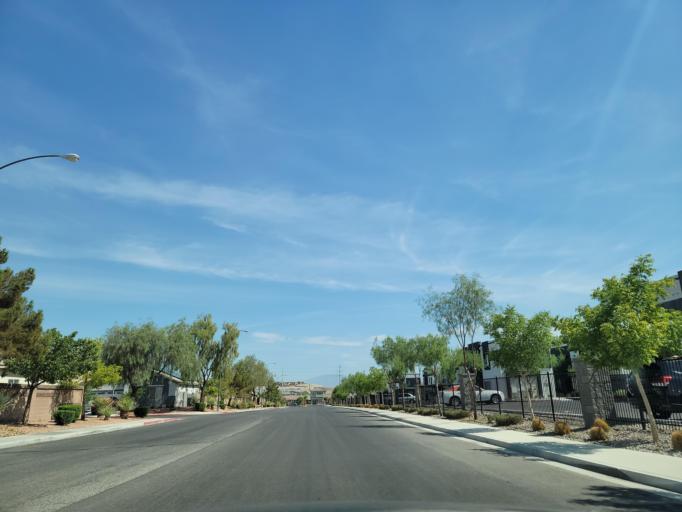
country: US
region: Nevada
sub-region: Clark County
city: Spring Valley
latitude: 36.0795
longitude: -115.2839
